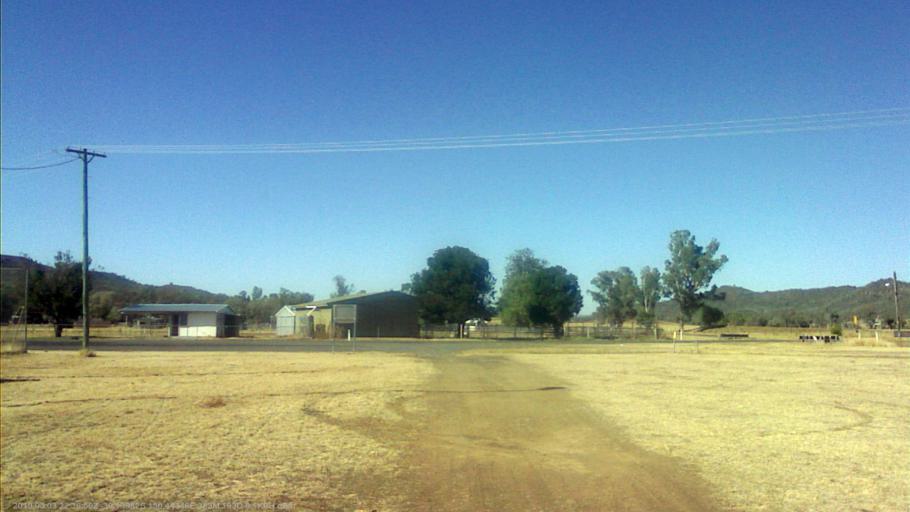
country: AU
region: New South Wales
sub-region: Gwydir
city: Bingara
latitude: -30.1398
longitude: 150.4434
